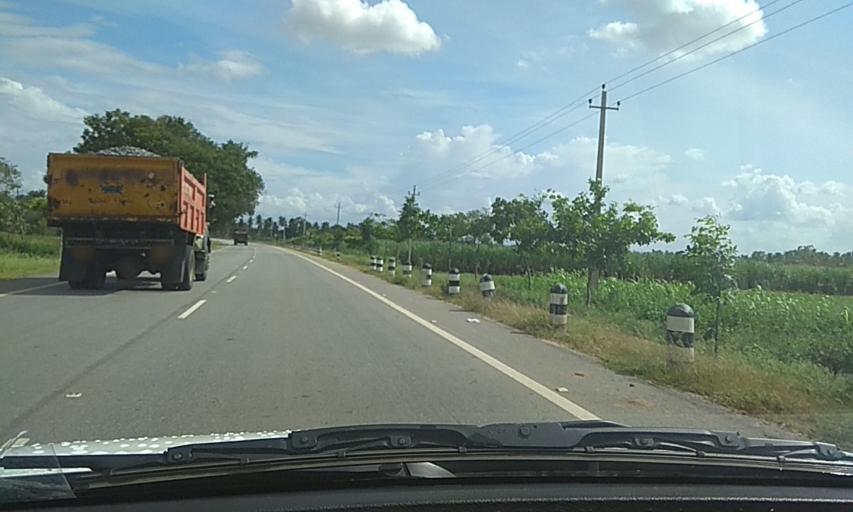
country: IN
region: Karnataka
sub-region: Mandya
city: Maddur
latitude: 12.6560
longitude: 77.0528
